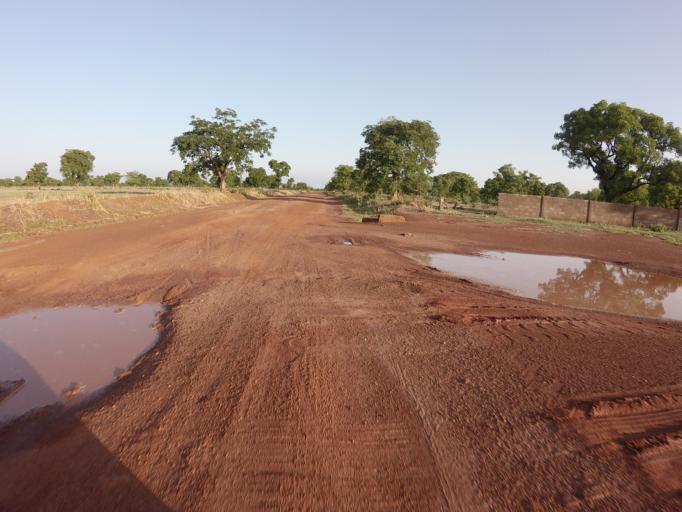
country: TG
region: Savanes
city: Sansanne-Mango
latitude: 10.2998
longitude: -0.0898
